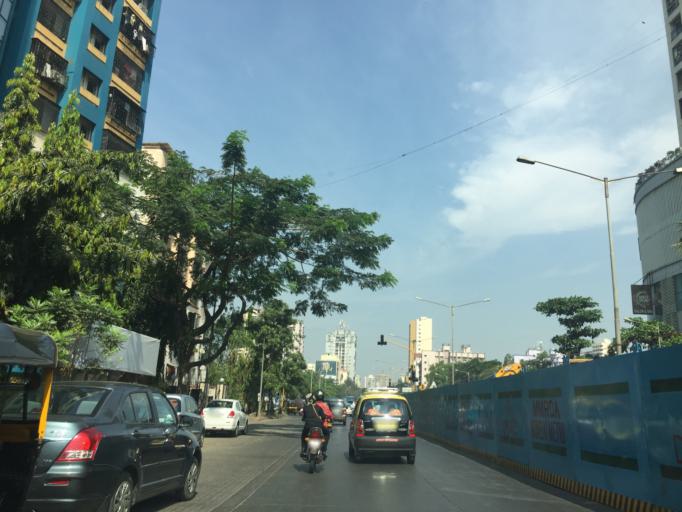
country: IN
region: Maharashtra
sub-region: Mumbai Suburban
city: Borivli
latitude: 19.2232
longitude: 72.8408
